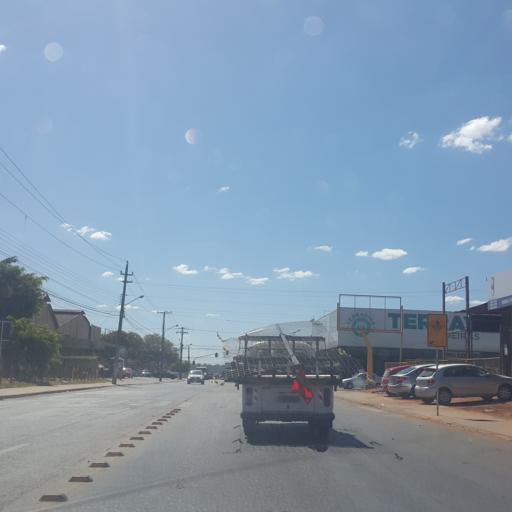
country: BR
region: Federal District
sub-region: Brasilia
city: Brasilia
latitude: -15.8067
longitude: -48.0743
